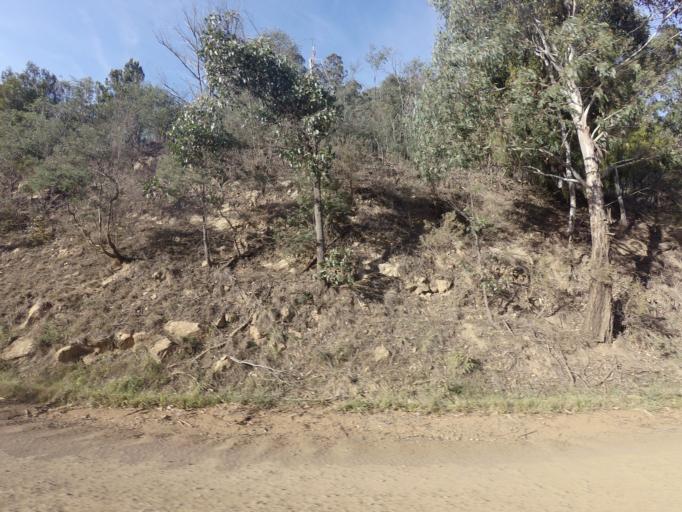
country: AU
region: Tasmania
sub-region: Sorell
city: Sorell
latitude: -42.4977
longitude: 147.4323
